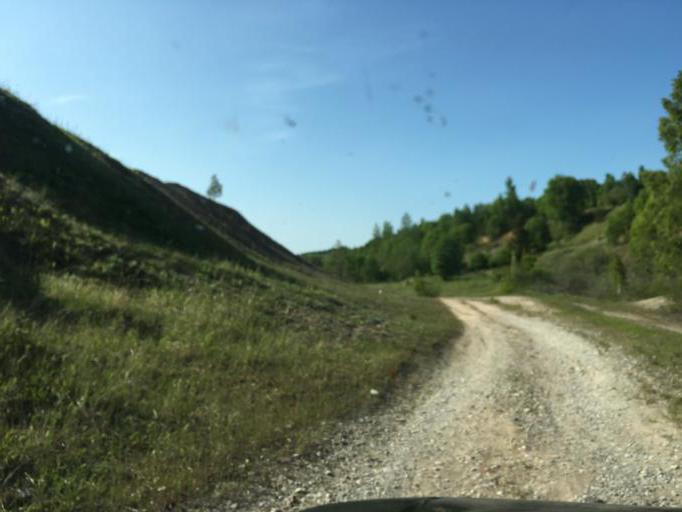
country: LV
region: Dundaga
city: Dundaga
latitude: 57.6115
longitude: 22.4404
